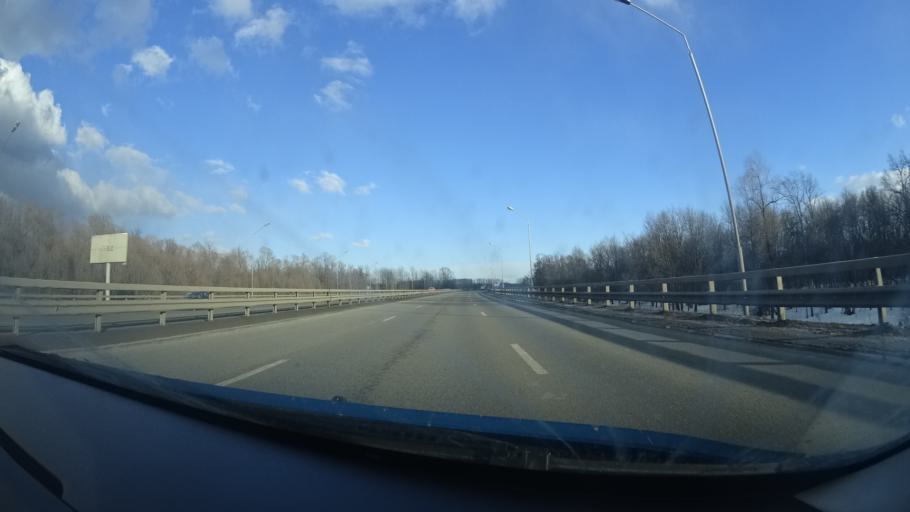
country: RU
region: Bashkortostan
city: Ufa
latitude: 54.6595
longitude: 55.8839
